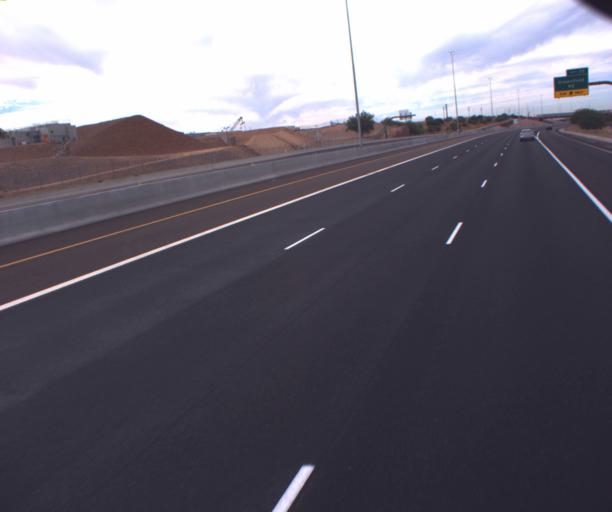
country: US
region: Arizona
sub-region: Maricopa County
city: Mesa
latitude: 33.4813
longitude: -111.7278
